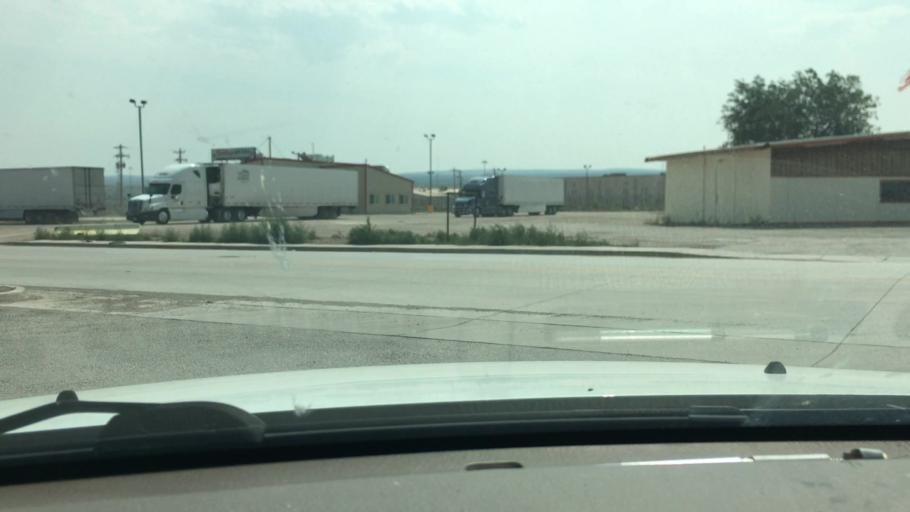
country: US
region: New Mexico
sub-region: Cibola County
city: Milan
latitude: 35.1814
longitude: -107.9046
